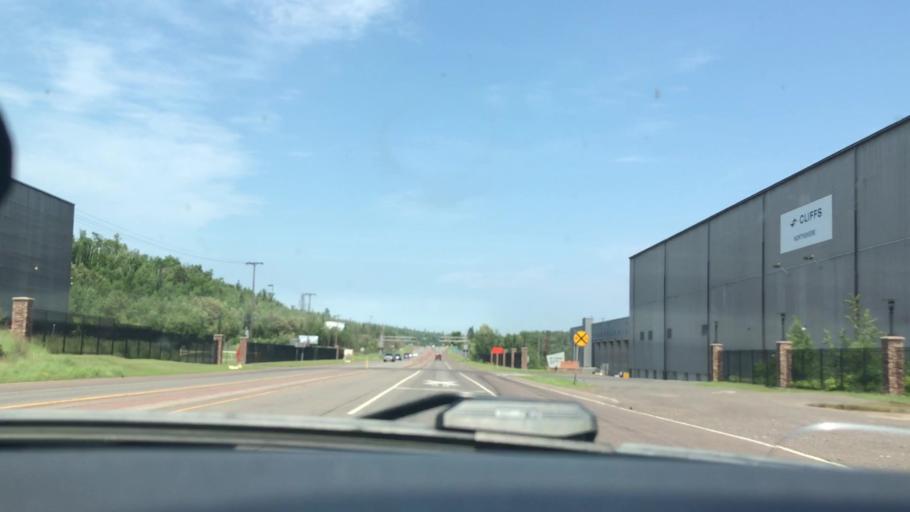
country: US
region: Minnesota
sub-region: Lake County
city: Silver Bay
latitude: 47.2891
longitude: -91.2631
